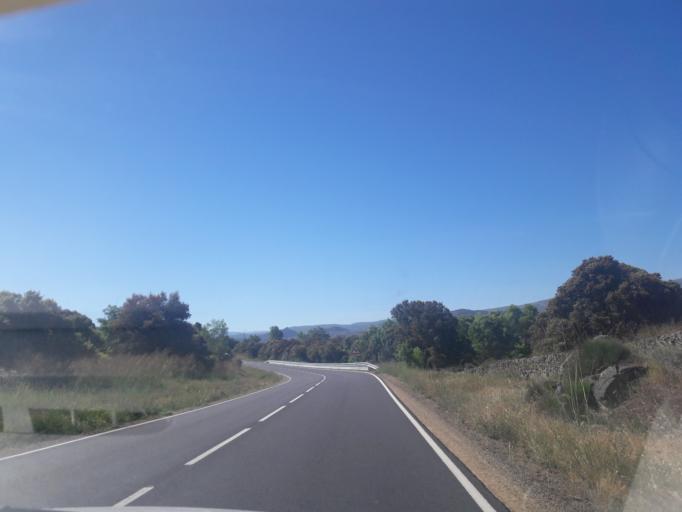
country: ES
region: Castille and Leon
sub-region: Provincia de Salamanca
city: Nava de Bejar
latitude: 40.4870
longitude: -5.6542
